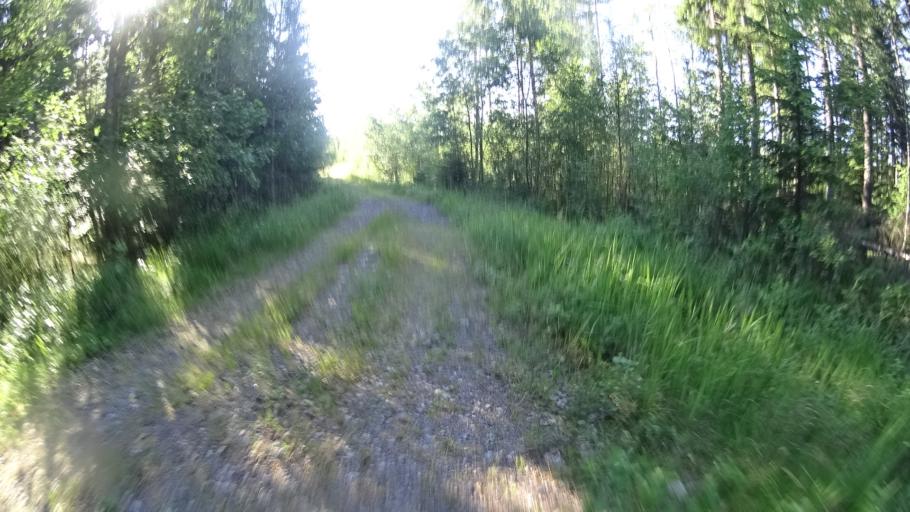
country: FI
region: Uusimaa
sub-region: Helsinki
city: Karkkila
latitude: 60.6541
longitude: 24.1414
